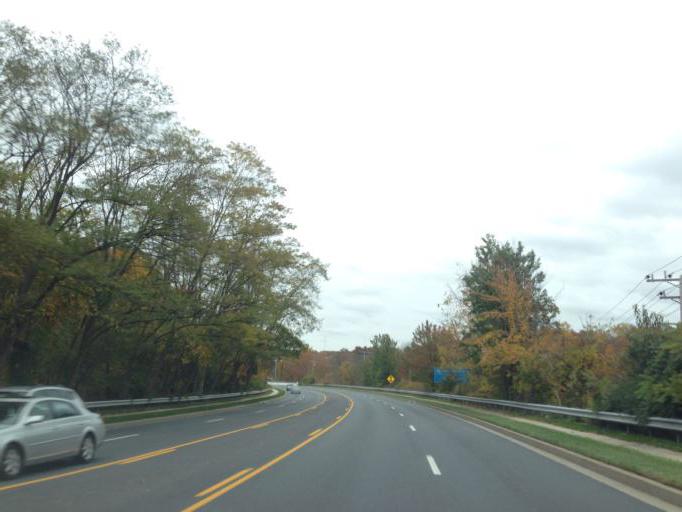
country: US
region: Maryland
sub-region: Baltimore County
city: Owings Mills
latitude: 39.4027
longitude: -76.7817
